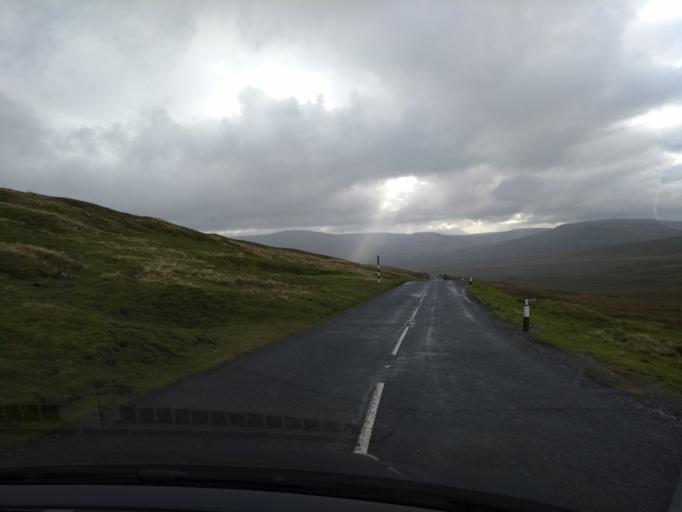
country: GB
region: England
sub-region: Cumbria
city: Kirkby Stephen
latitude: 54.3446
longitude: -2.2042
